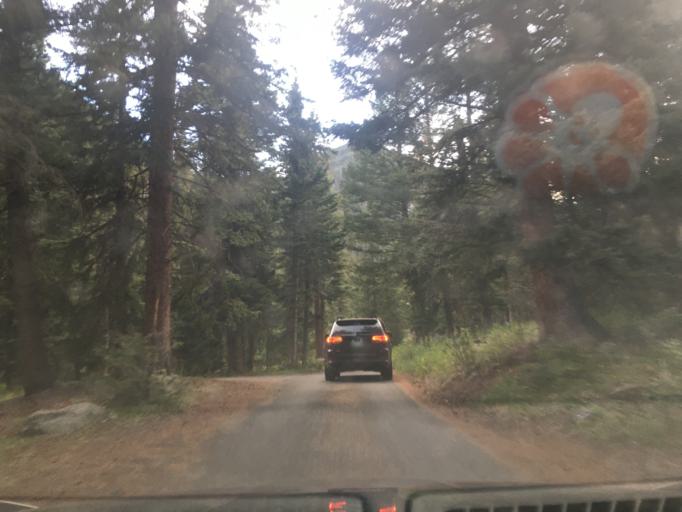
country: US
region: Colorado
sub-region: Larimer County
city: Estes Park
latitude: 40.4138
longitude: -105.6587
